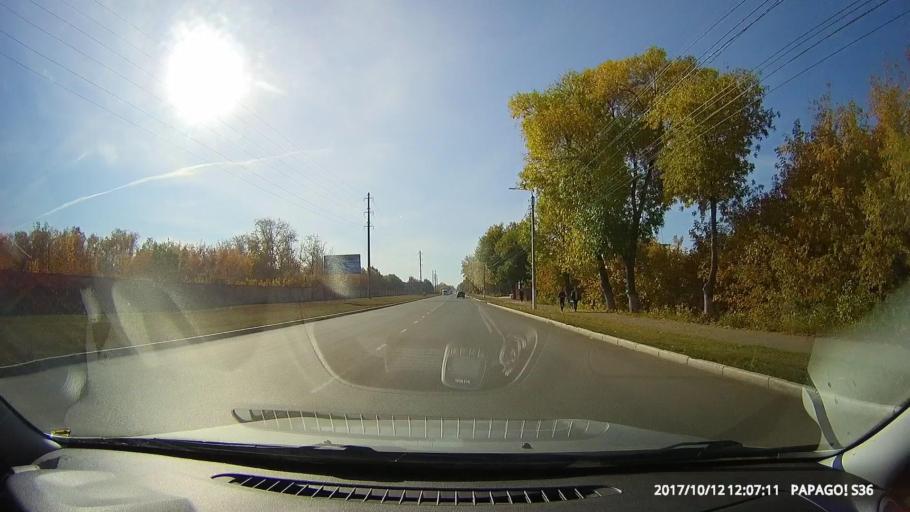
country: RU
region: Samara
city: Chapayevsk
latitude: 52.9686
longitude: 49.7029
